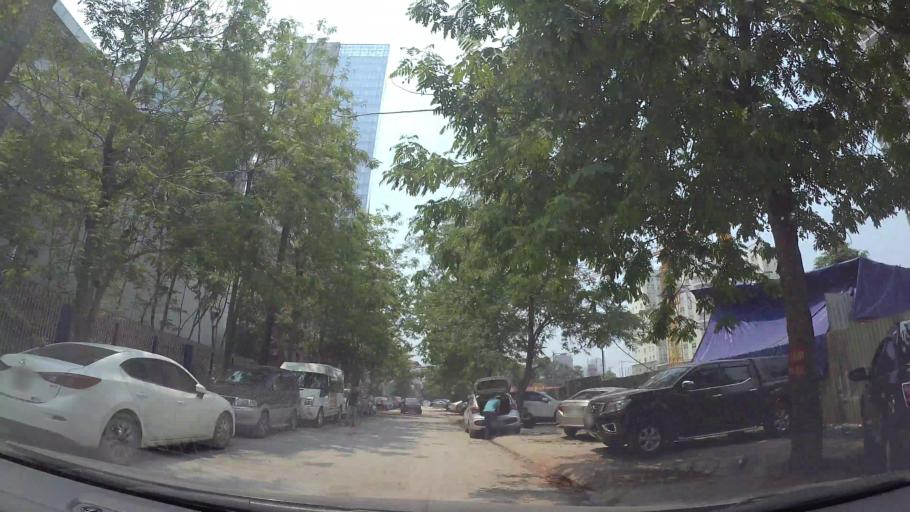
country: VN
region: Ha Noi
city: Thanh Xuan
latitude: 21.0078
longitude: 105.7994
